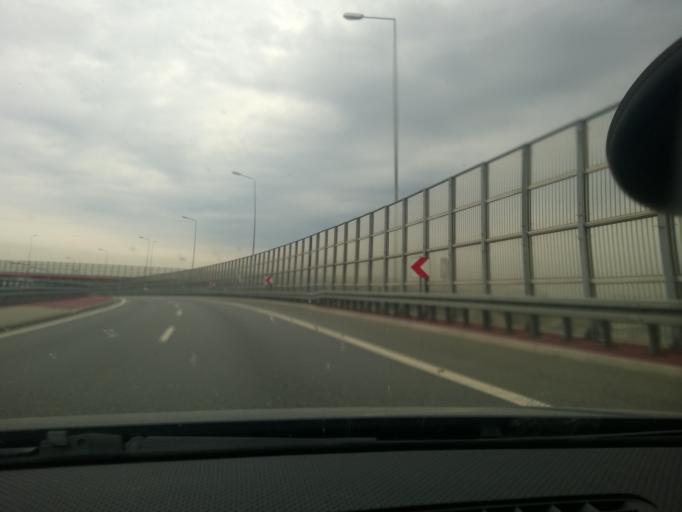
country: PL
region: Masovian Voivodeship
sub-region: Powiat pruszkowski
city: Piastow
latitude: 52.2000
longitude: 20.8411
